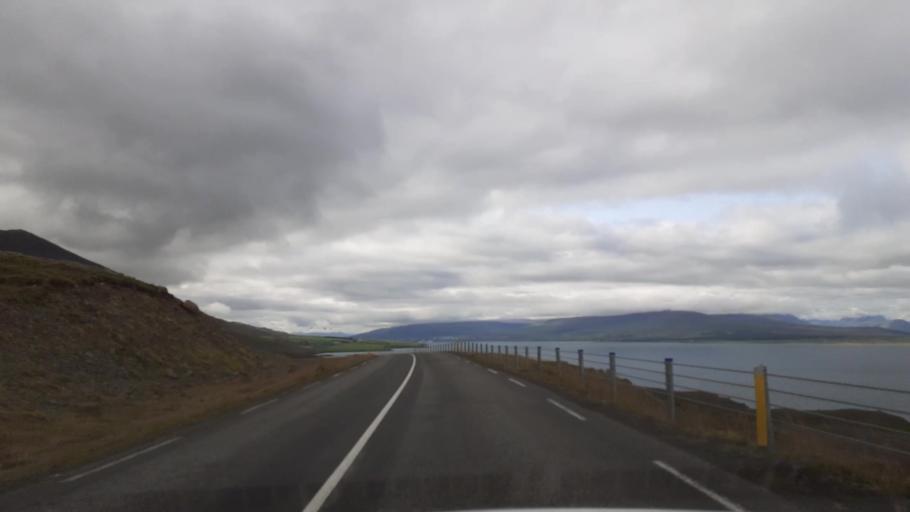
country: IS
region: Northeast
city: Akureyri
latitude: 65.8300
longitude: -18.0578
